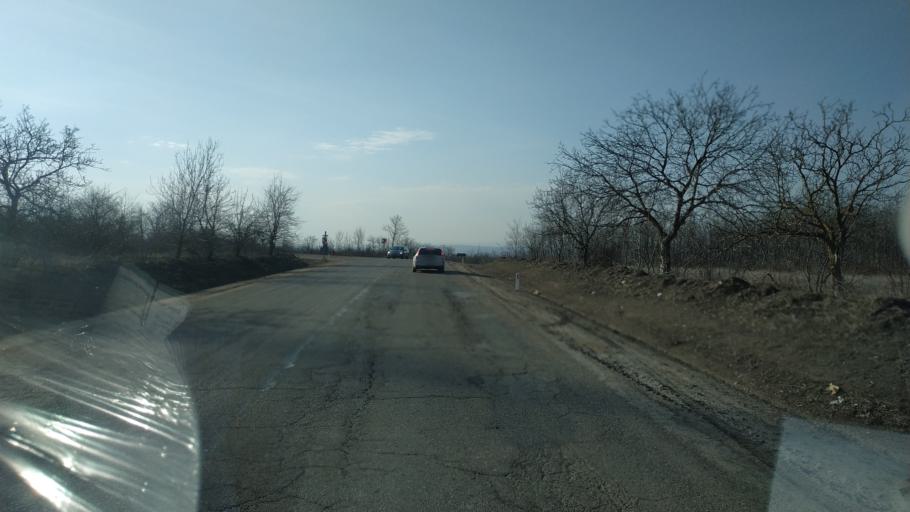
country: MD
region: Chisinau
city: Singera
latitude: 46.8590
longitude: 29.0315
